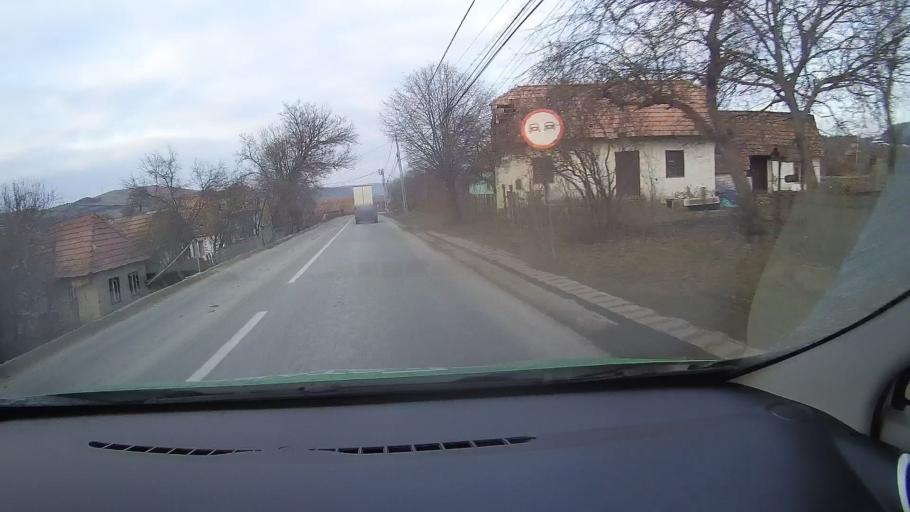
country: RO
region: Harghita
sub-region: Comuna Simonesti
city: Simonesti
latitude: 46.3424
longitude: 25.1149
